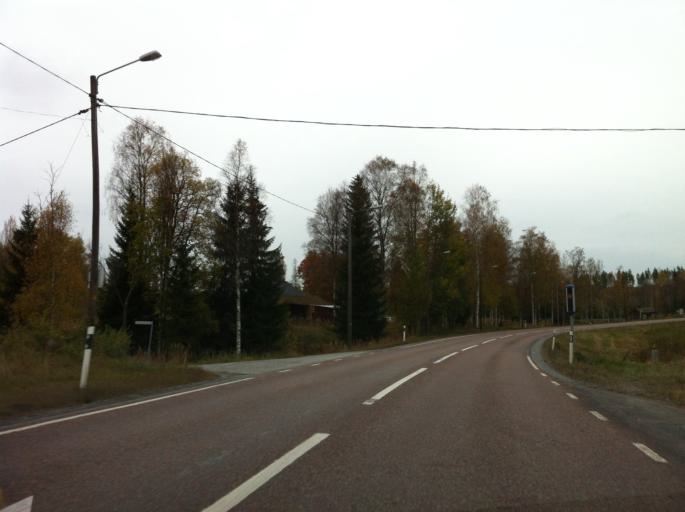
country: SE
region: Dalarna
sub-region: Ludvika Kommun
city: Grangesberg
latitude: 60.0327
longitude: 14.9722
